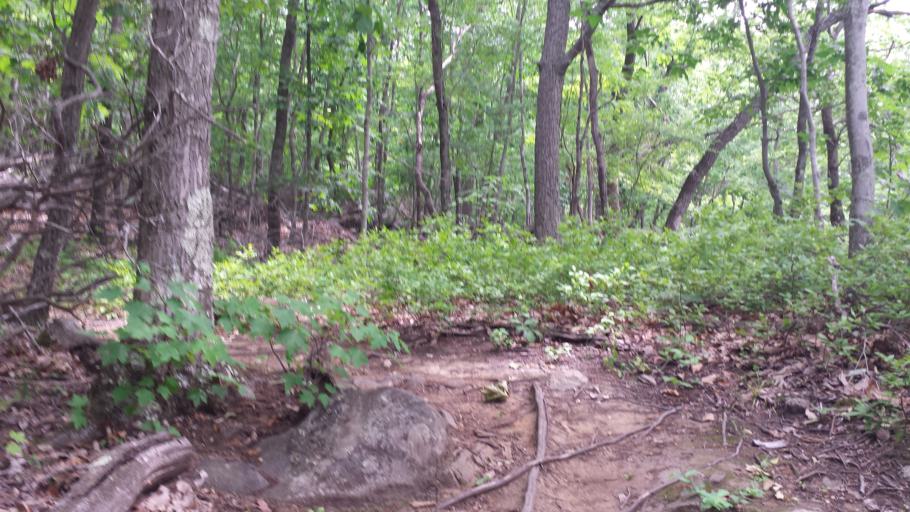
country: US
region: New York
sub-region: Putnam County
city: Peach Lake
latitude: 41.3031
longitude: -73.5648
